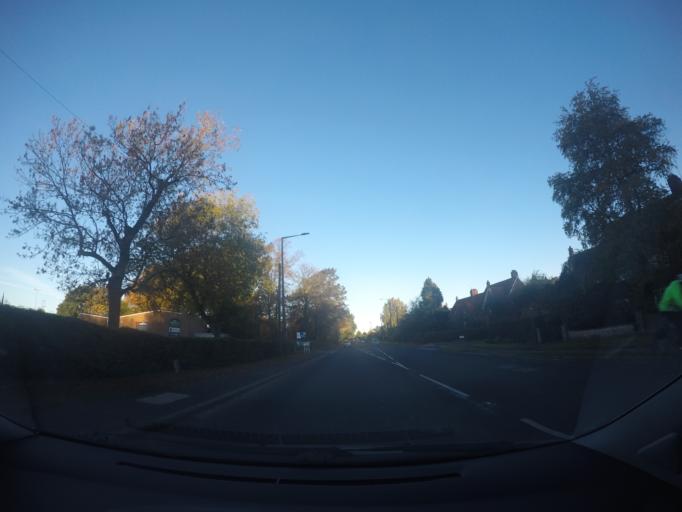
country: GB
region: England
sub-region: City of York
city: York
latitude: 53.9728
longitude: -1.1044
